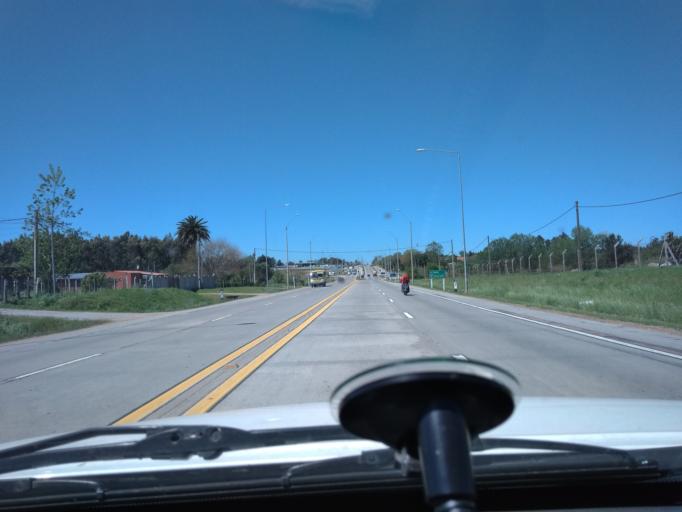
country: UY
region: Canelones
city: La Paz
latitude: -34.7975
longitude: -56.1565
